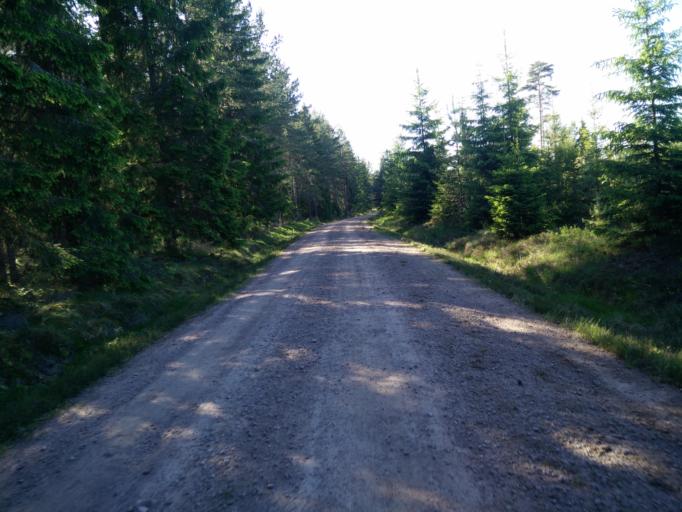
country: SE
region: Vaermland
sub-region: Hagfors Kommun
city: Hagfors
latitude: 60.0207
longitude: 13.5596
